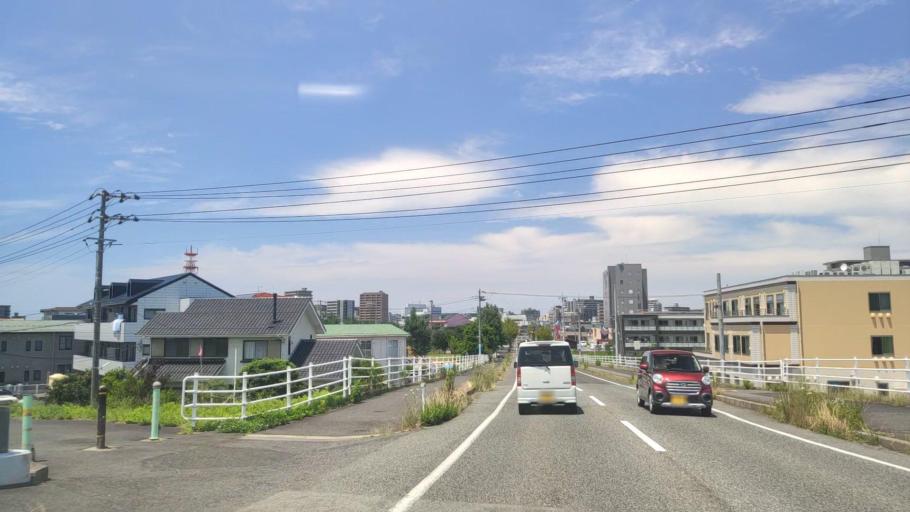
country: JP
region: Tottori
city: Tottori
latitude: 35.4840
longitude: 134.2341
